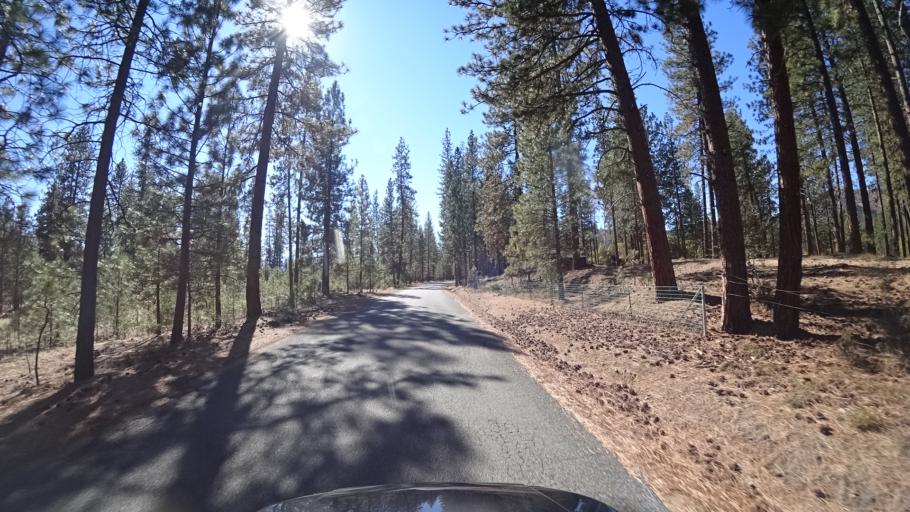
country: US
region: California
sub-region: Siskiyou County
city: Yreka
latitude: 41.5832
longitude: -122.9131
